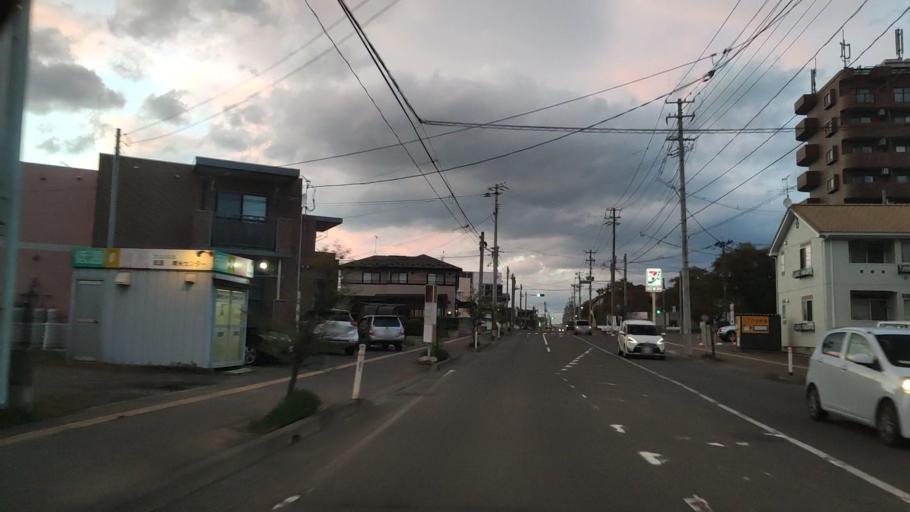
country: JP
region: Iwate
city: Morioka-shi
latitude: 39.7214
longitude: 141.1091
